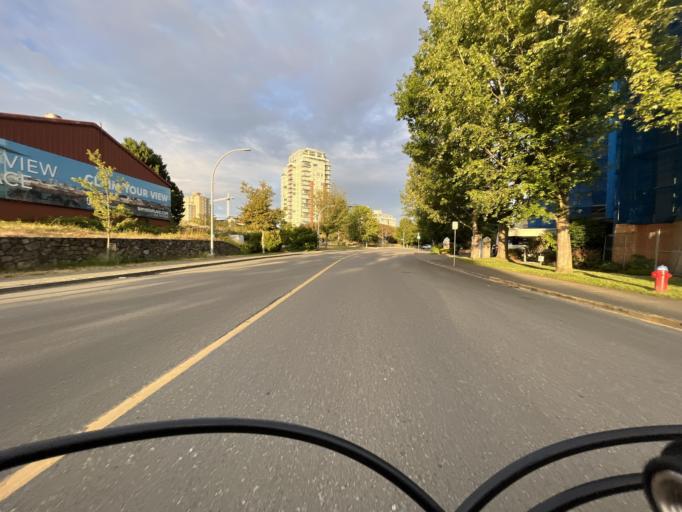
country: CA
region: British Columbia
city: Victoria
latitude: 48.4290
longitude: -123.3829
